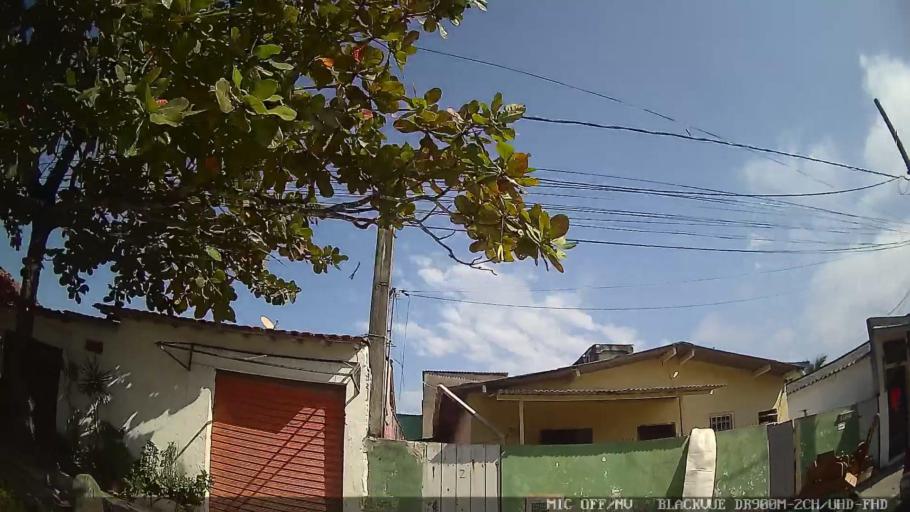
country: BR
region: Sao Paulo
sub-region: Guaruja
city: Guaruja
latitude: -23.9781
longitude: -46.1948
